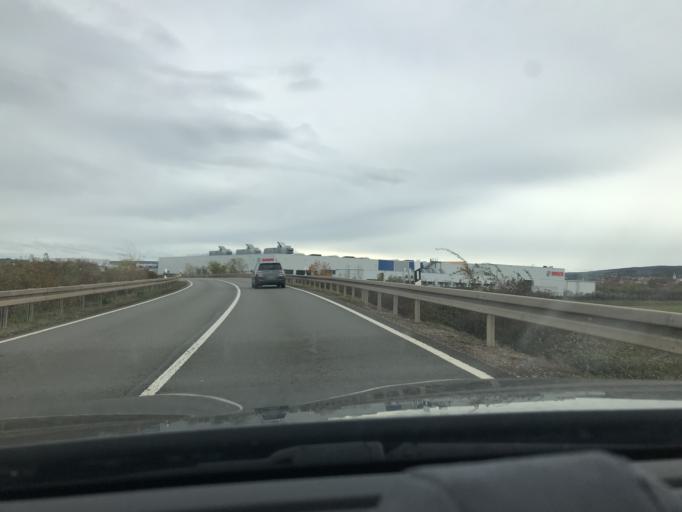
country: DE
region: Thuringia
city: Arnstadt
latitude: 50.8538
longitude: 10.9437
